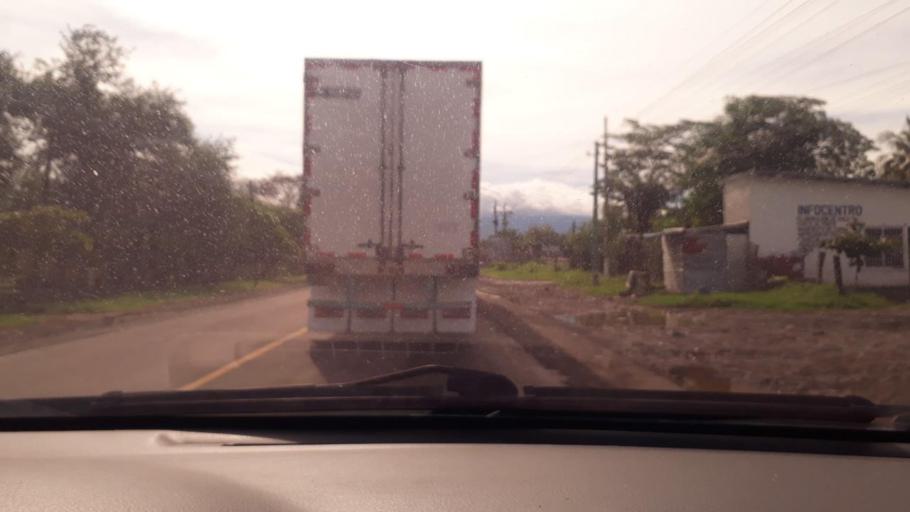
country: SV
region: Ahuachapan
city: San Francisco Menendez
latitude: 13.8797
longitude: -90.1108
